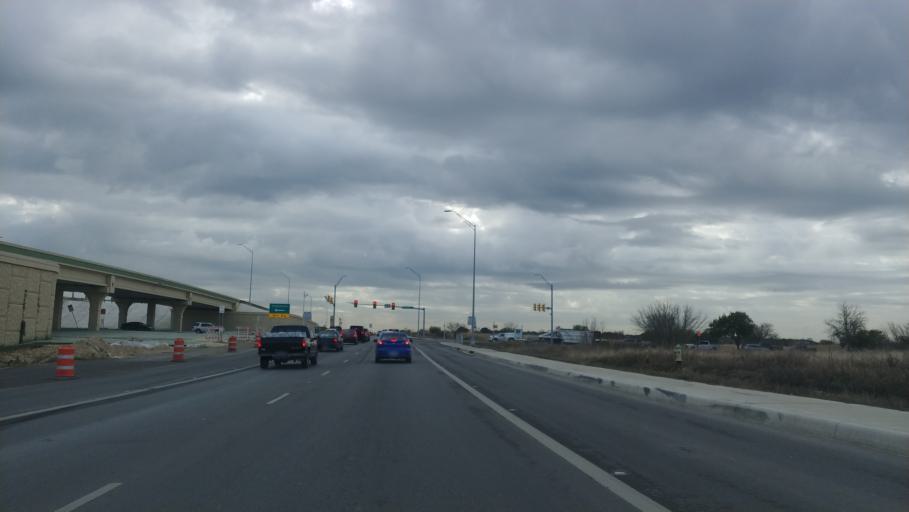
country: US
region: Texas
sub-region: Bexar County
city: Lackland Air Force Base
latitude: 29.4039
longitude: -98.7081
